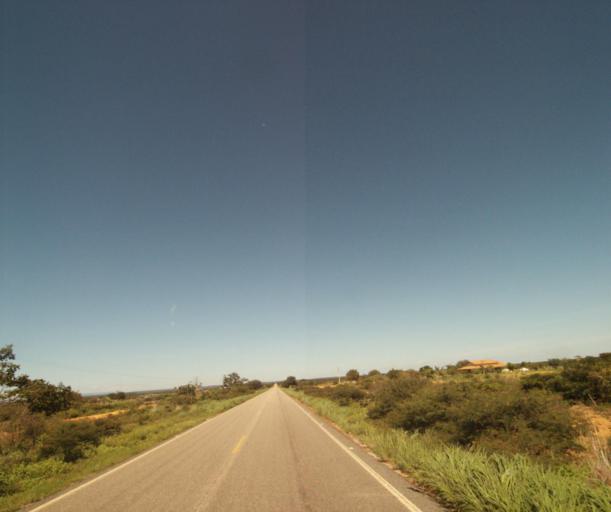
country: BR
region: Bahia
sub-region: Palmas De Monte Alto
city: Palmas de Monte Alto
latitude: -14.2560
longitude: -43.2432
